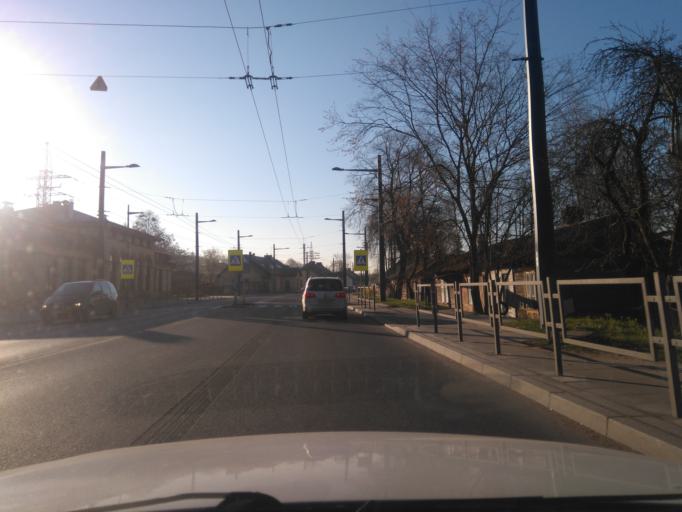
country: LT
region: Kauno apskritis
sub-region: Kaunas
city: Aleksotas
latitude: 54.8802
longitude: 23.9306
